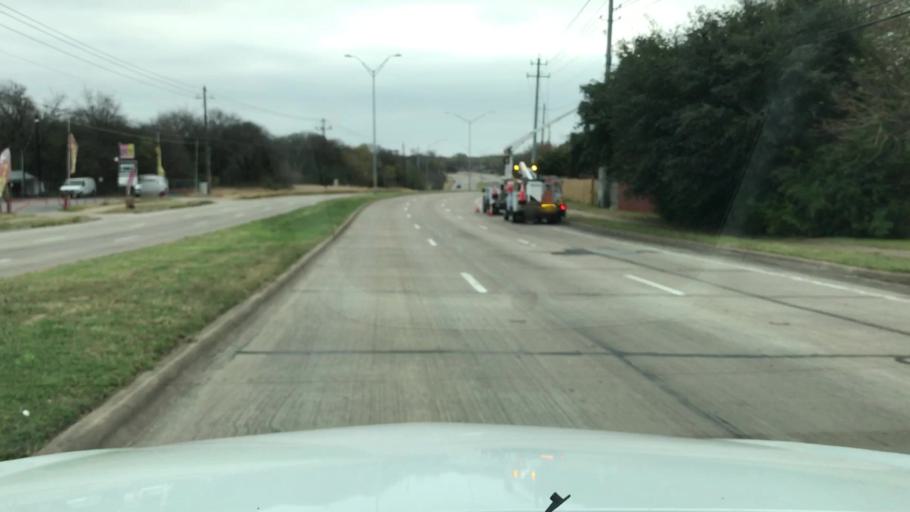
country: US
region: Texas
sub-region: Travis County
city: Onion Creek
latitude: 30.1841
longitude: -97.7550
